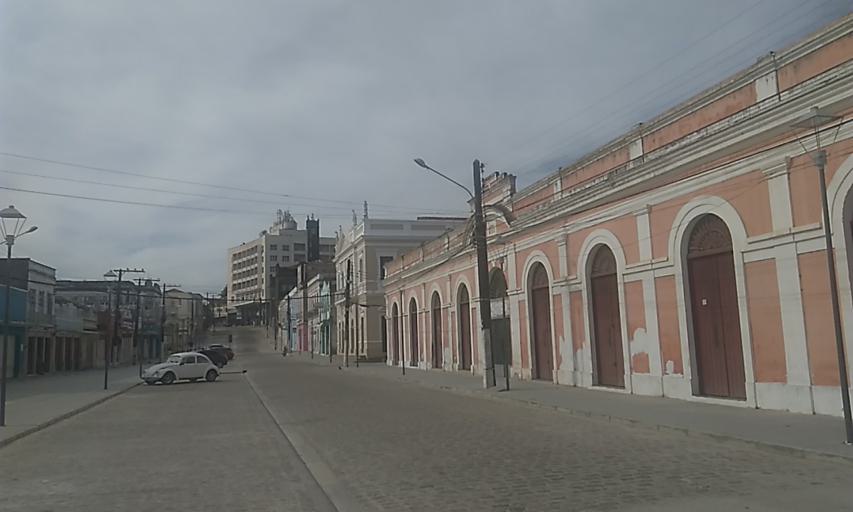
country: BR
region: Alagoas
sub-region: Penedo
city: Penedo
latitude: -10.2919
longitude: -36.5847
